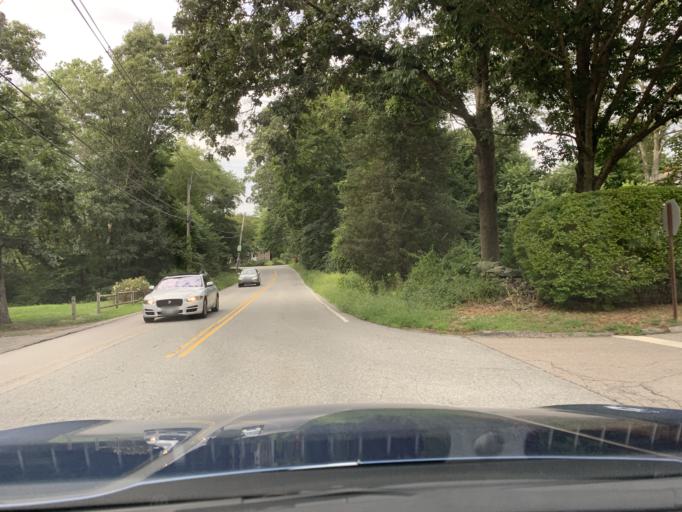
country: US
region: Rhode Island
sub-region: Kent County
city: East Greenwich
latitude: 41.6260
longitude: -71.4483
